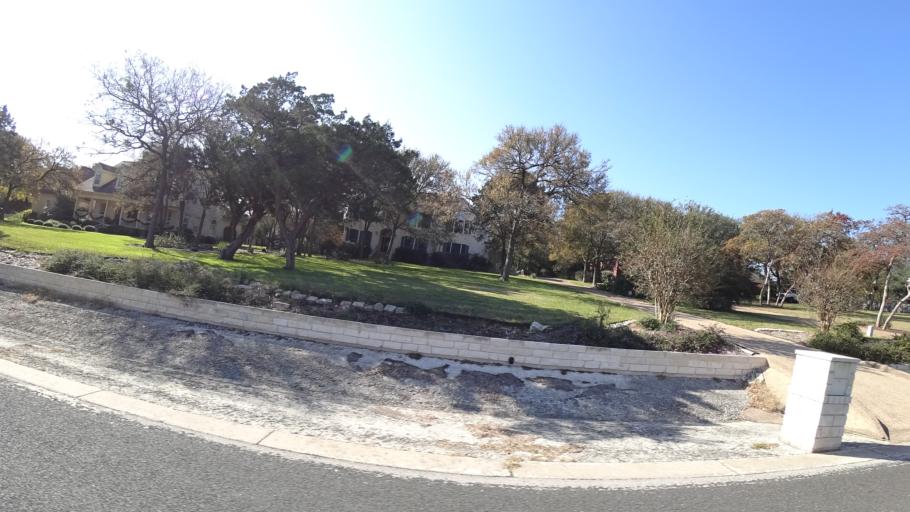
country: US
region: Texas
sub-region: Williamson County
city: Anderson Mill
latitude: 30.3820
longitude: -97.8280
